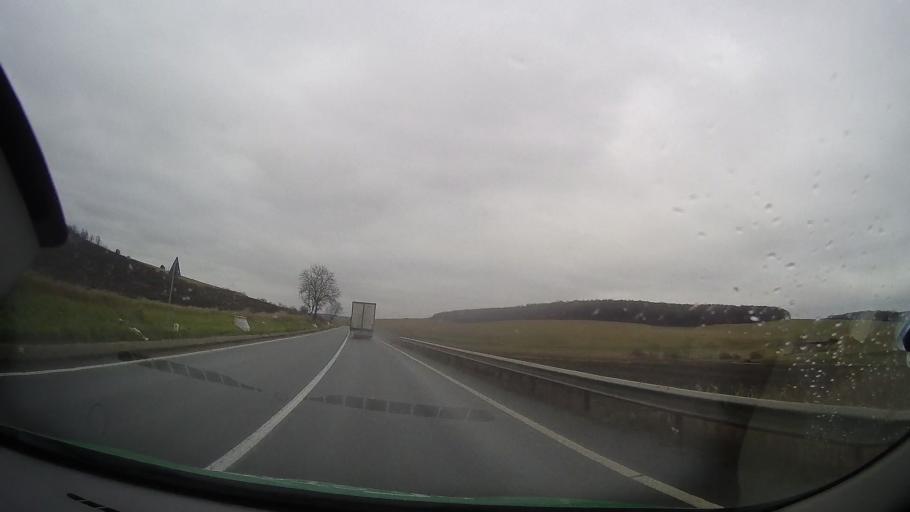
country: RO
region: Mures
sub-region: Comuna Lunca
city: Lunca
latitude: 46.8620
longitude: 24.5545
